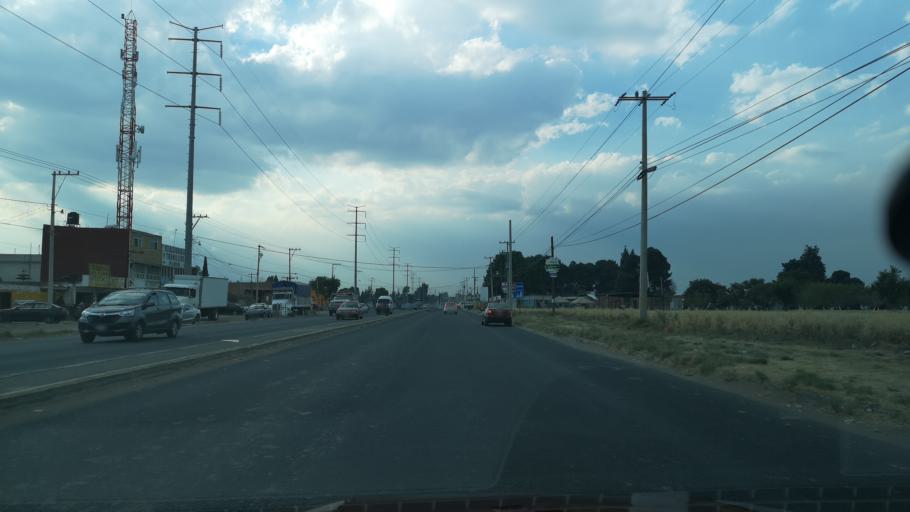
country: MX
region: Puebla
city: Cuanala
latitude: 19.0880
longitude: -98.3338
